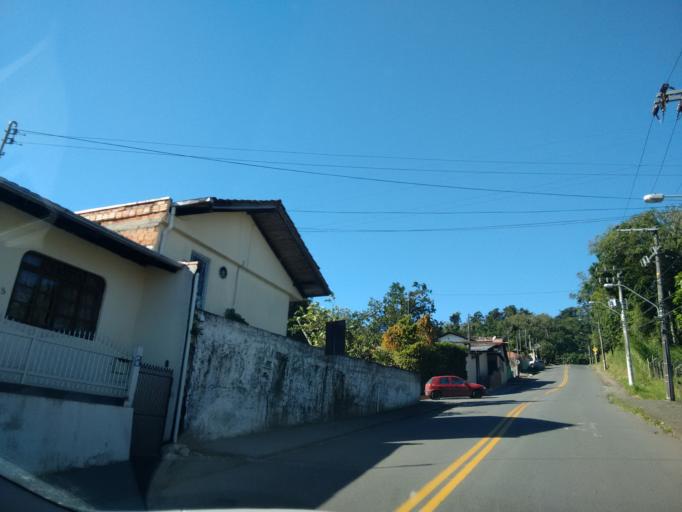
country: BR
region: Santa Catarina
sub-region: Blumenau
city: Blumenau
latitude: -26.8876
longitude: -49.1126
